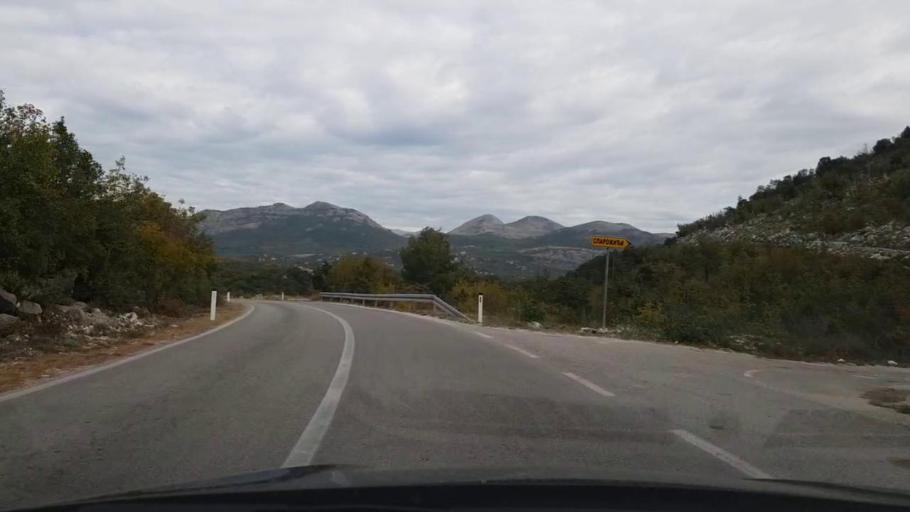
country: HR
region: Dubrovacko-Neretvanska
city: Cibaca
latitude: 42.6701
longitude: 18.2280
